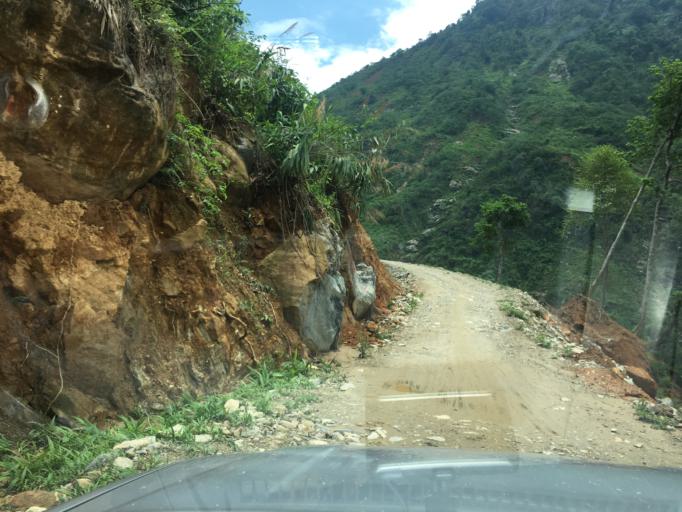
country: VN
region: Yen Bai
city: Son Thinh
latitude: 21.6819
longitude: 104.5608
